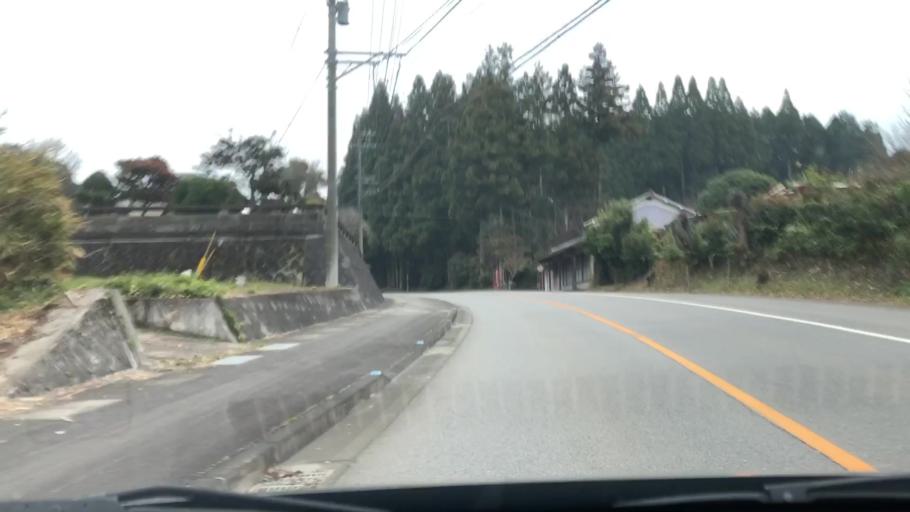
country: JP
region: Oita
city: Usuki
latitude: 33.0056
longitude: 131.6496
